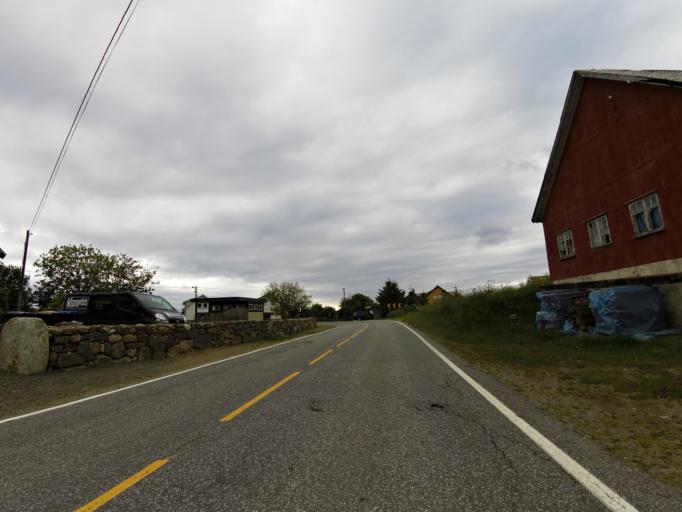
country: NO
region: Vest-Agder
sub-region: Farsund
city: Vestbygd
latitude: 58.1214
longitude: 6.6007
